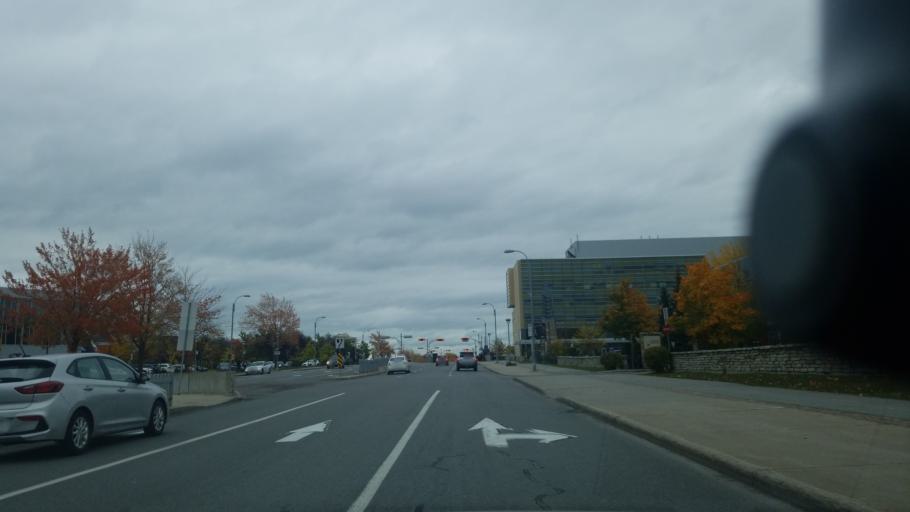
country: CA
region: Quebec
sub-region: Laval
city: Laval
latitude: 45.5608
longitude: -73.7218
